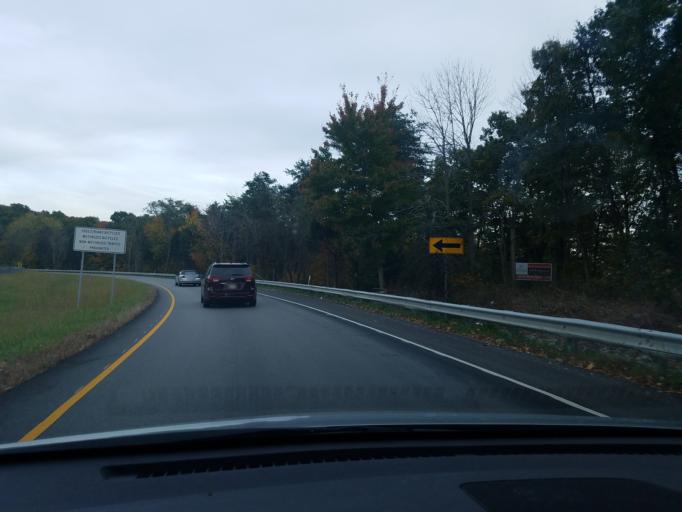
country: US
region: Indiana
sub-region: Floyd County
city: New Albany
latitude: 38.3026
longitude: -85.8896
